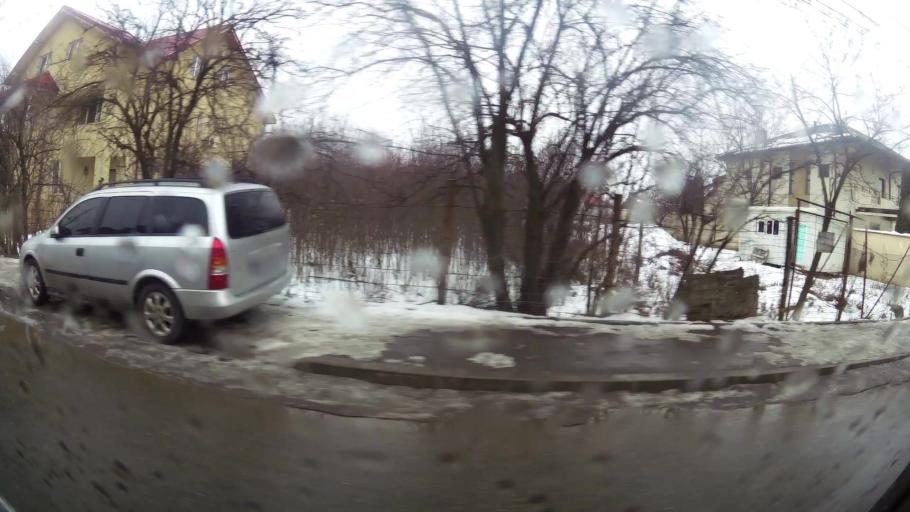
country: RO
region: Ilfov
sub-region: Comuna Chiajna
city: Rosu
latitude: 44.4089
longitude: 26.0109
